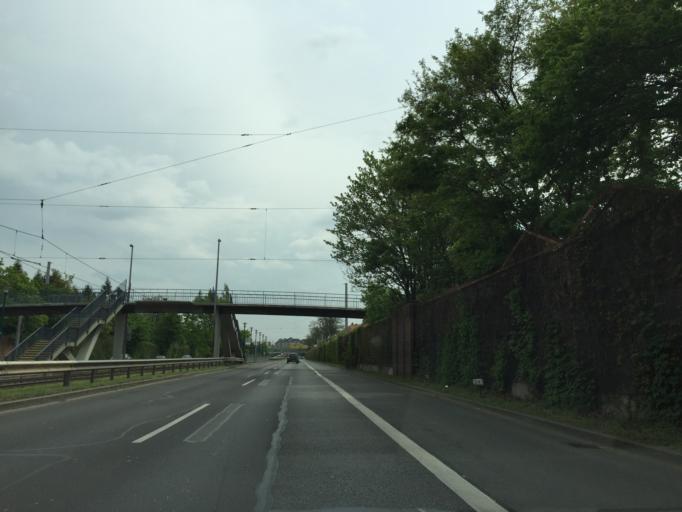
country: DE
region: Rheinland-Pfalz
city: Altrip
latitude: 49.4435
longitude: 8.5147
